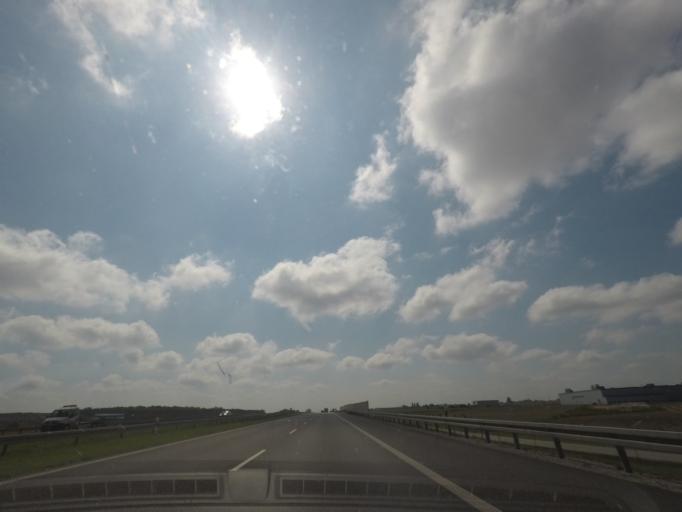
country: PL
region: Kujawsko-Pomorskie
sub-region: Powiat wloclawski
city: Brzesc Kujawski
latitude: 52.6402
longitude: 18.9484
